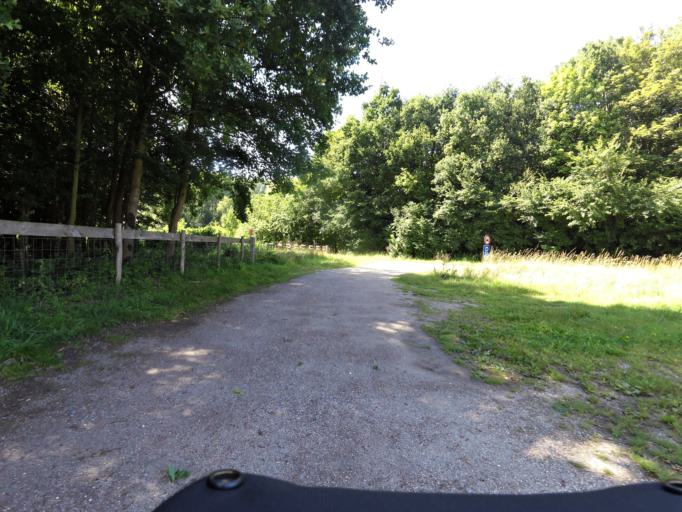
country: NL
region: Zeeland
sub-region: Gemeente Noord-Beveland
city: Kamperland
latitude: 51.5359
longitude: 3.7088
